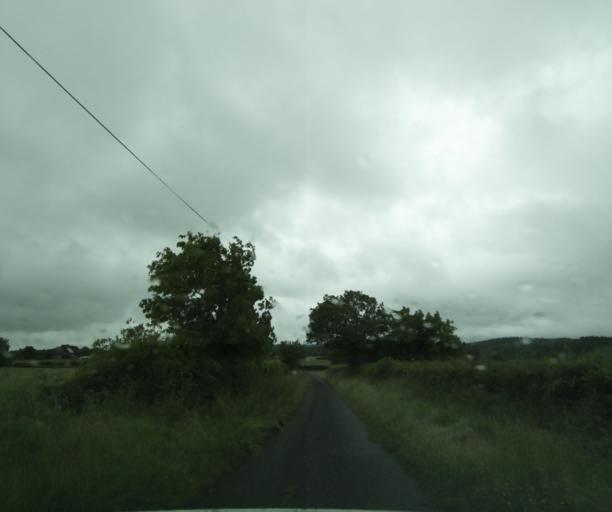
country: FR
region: Bourgogne
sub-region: Departement de Saone-et-Loire
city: Saint-Vallier
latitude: 46.5178
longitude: 4.3900
